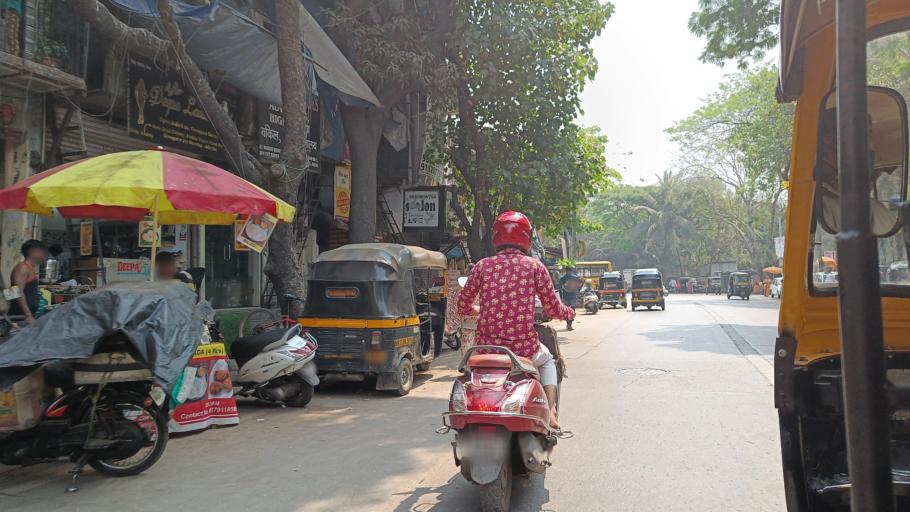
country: IN
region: Maharashtra
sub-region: Mumbai Suburban
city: Powai
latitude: 19.1536
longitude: 72.8392
